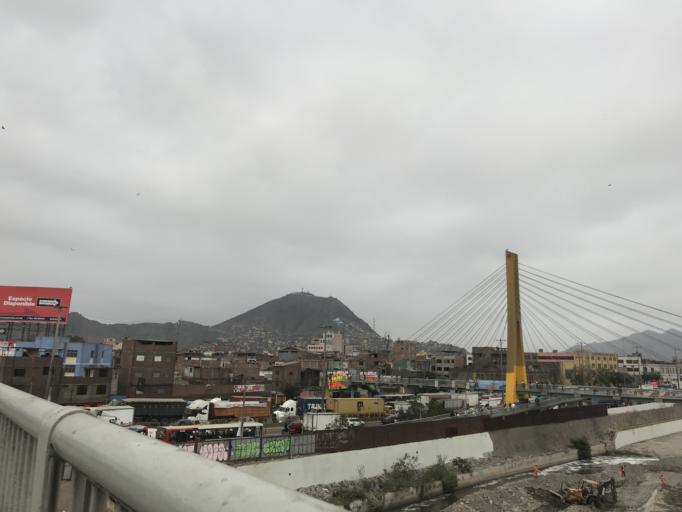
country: PE
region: Lima
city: Lima
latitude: -12.0415
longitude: -77.0341
